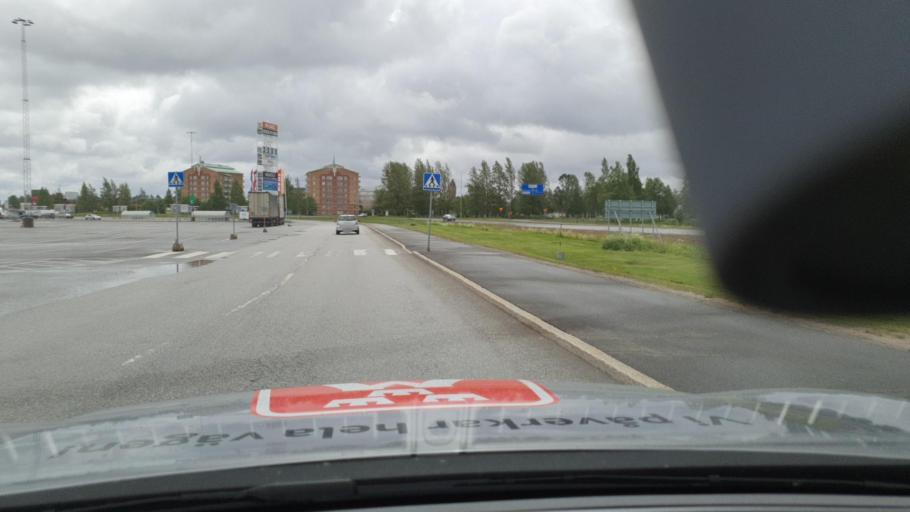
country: SE
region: Norrbotten
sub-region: Haparanda Kommun
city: Haparanda
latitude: 65.8440
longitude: 24.1262
